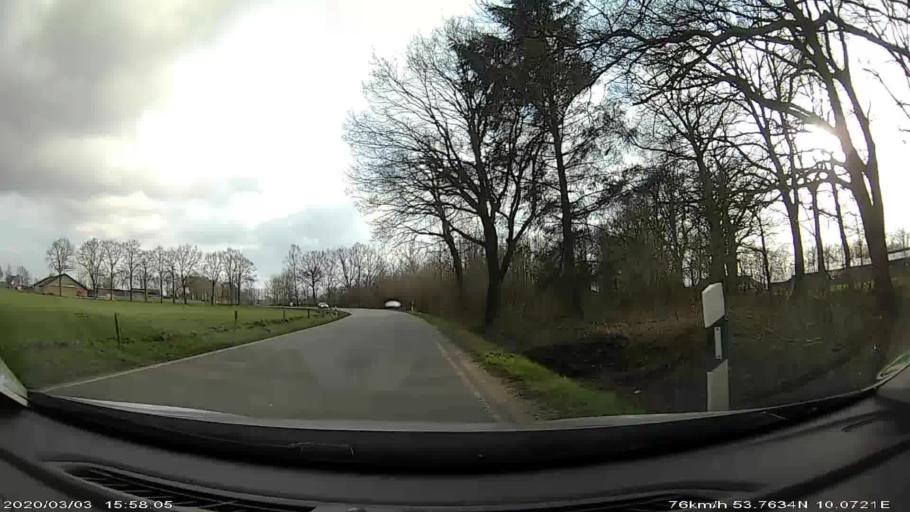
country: DE
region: Schleswig-Holstein
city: Tangstedt
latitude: 53.7651
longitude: 10.0726
